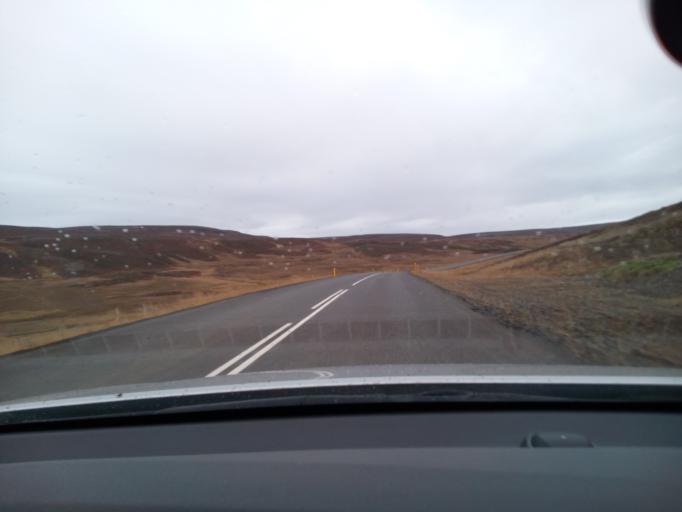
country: IS
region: Northeast
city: Laugar
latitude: 65.7980
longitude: -17.2482
